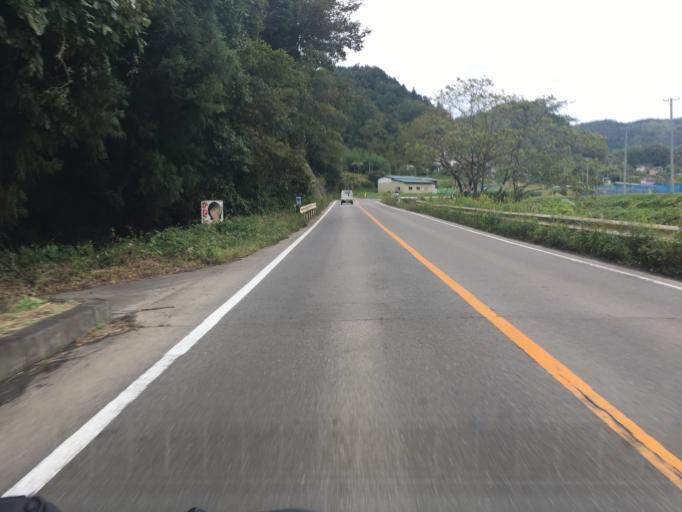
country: JP
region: Fukushima
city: Yanagawamachi-saiwaicho
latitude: 37.8740
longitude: 140.6463
